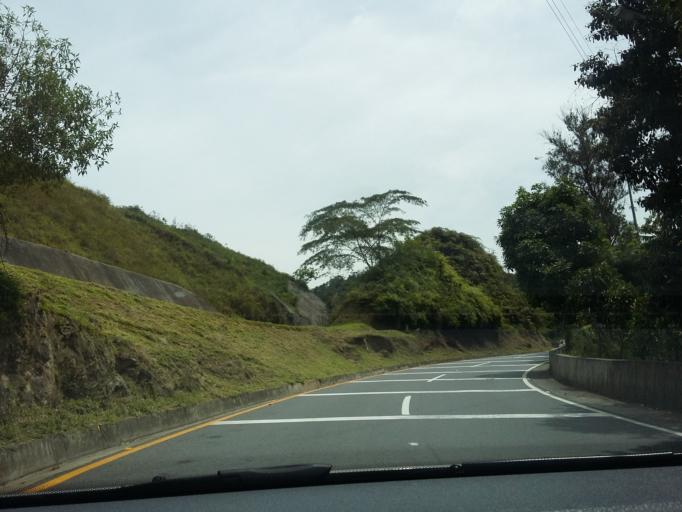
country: CO
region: Santander
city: Bucaramanga
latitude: 7.1101
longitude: -73.0784
